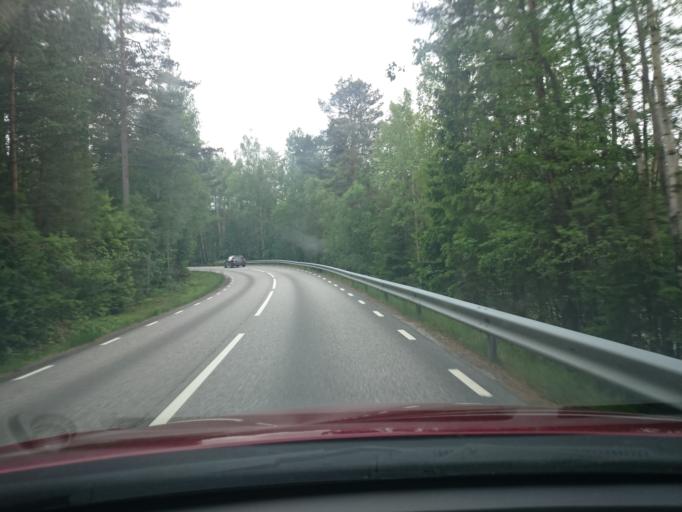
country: SE
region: Vaestra Goetaland
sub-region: Lerums Kommun
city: Stenkullen
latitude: 57.7514
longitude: 12.3280
